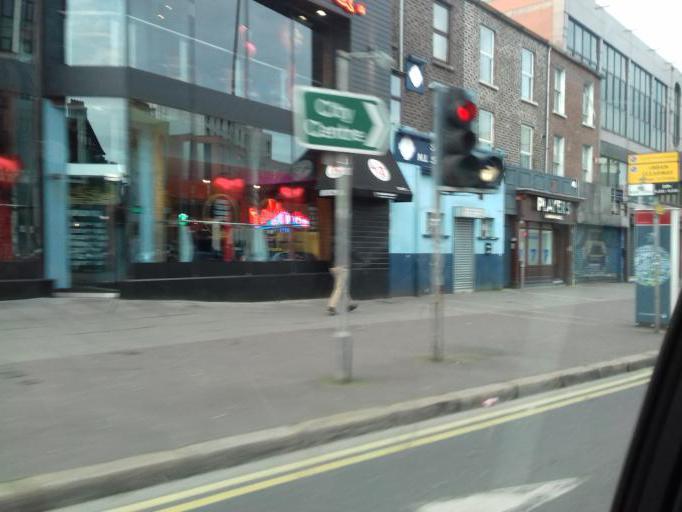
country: GB
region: Northern Ireland
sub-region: City of Belfast
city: Belfast
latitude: 54.5895
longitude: -5.9343
